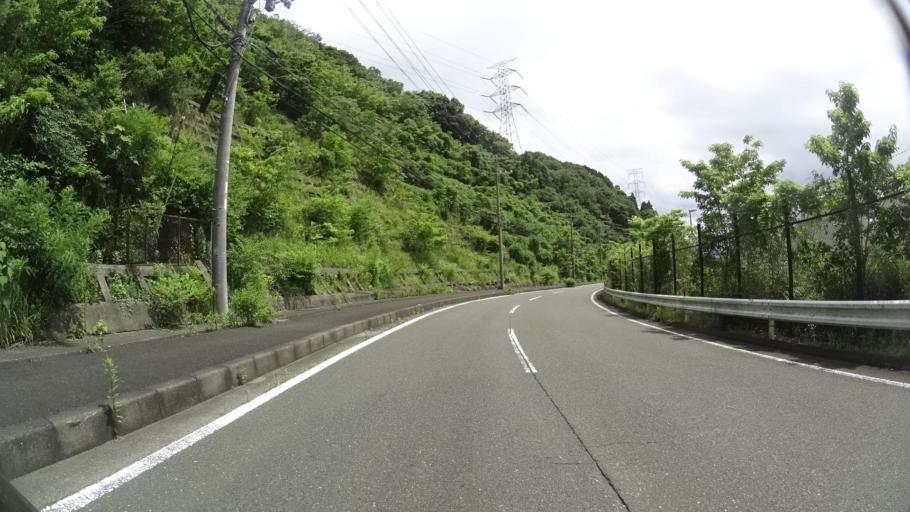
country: JP
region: Kyoto
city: Maizuru
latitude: 35.5321
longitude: 135.3471
